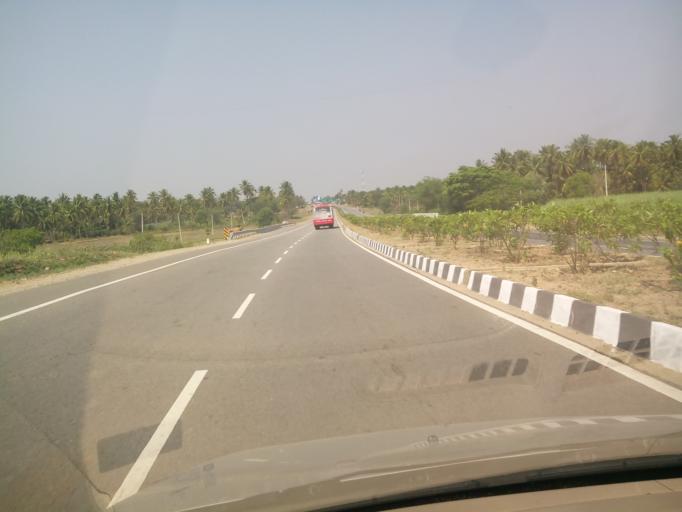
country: IN
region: Karnataka
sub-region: Hassan
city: Channarayapatna
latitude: 12.9087
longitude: 76.4354
